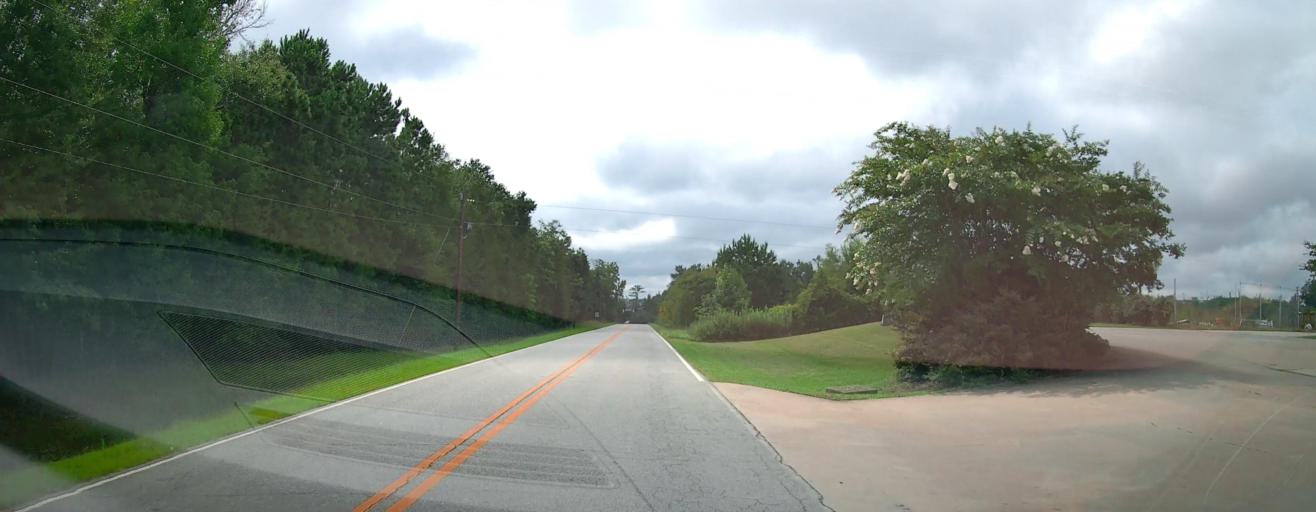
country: US
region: Georgia
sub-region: Bibb County
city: West Point
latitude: 32.8212
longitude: -83.7286
